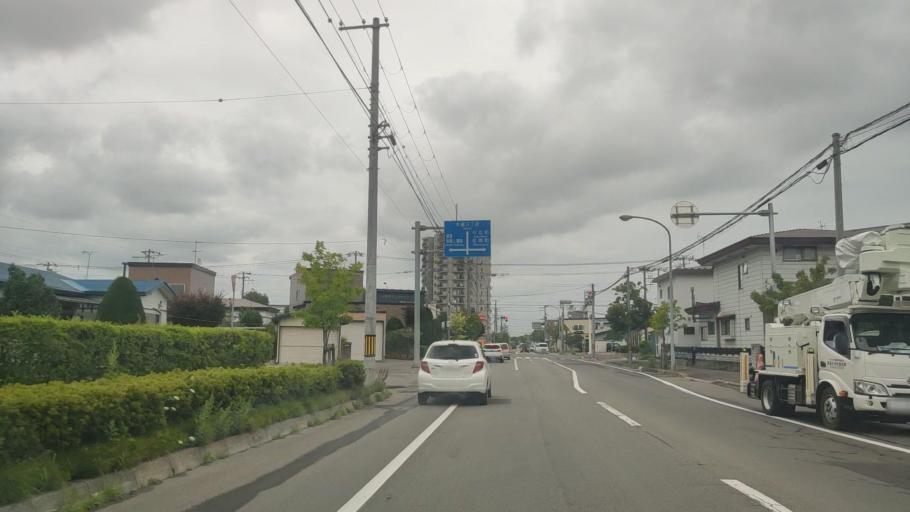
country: JP
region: Hokkaido
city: Hakodate
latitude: 41.7990
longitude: 140.7613
